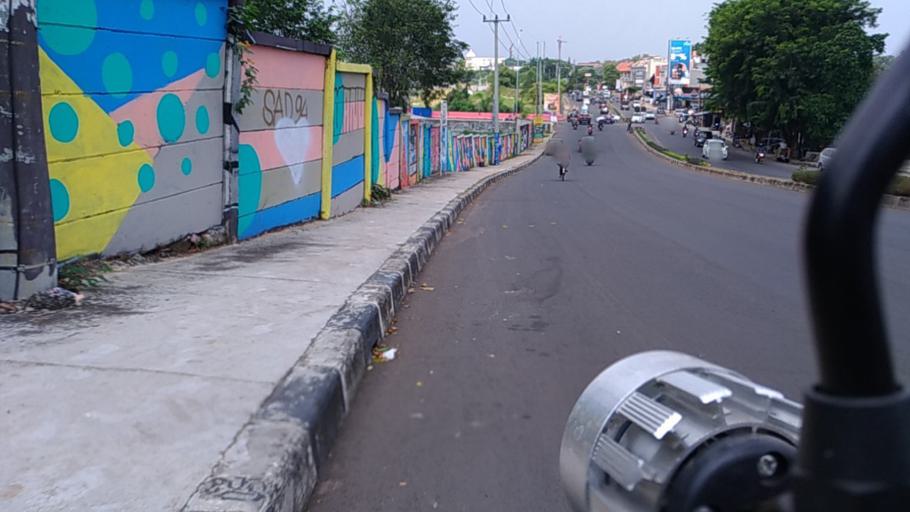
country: ID
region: West Java
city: Depok
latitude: -6.3781
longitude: 106.8356
